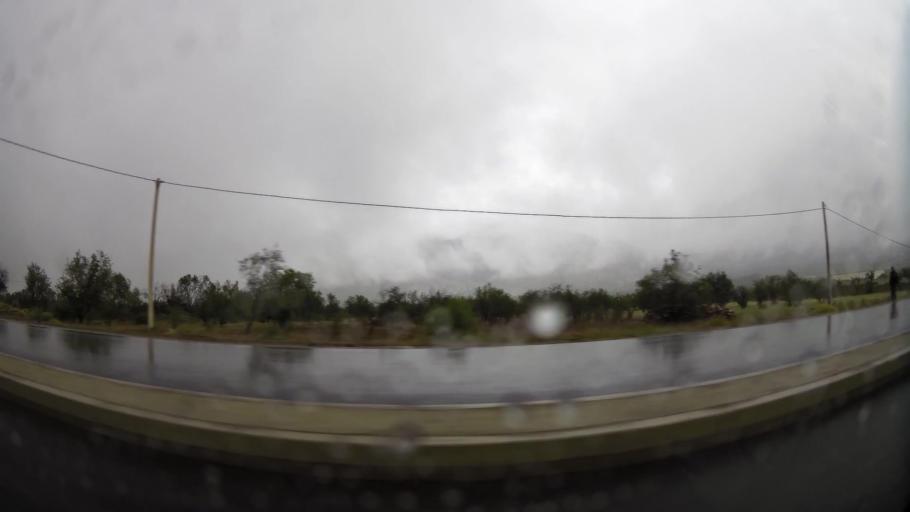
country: MA
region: Oriental
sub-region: Nador
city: Midar
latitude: 34.8441
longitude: -3.7213
